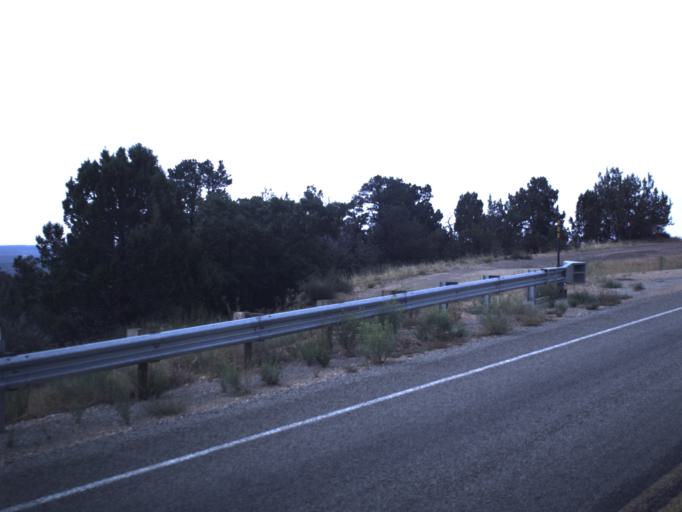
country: US
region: Utah
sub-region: Washington County
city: Hildale
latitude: 37.2525
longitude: -112.7970
